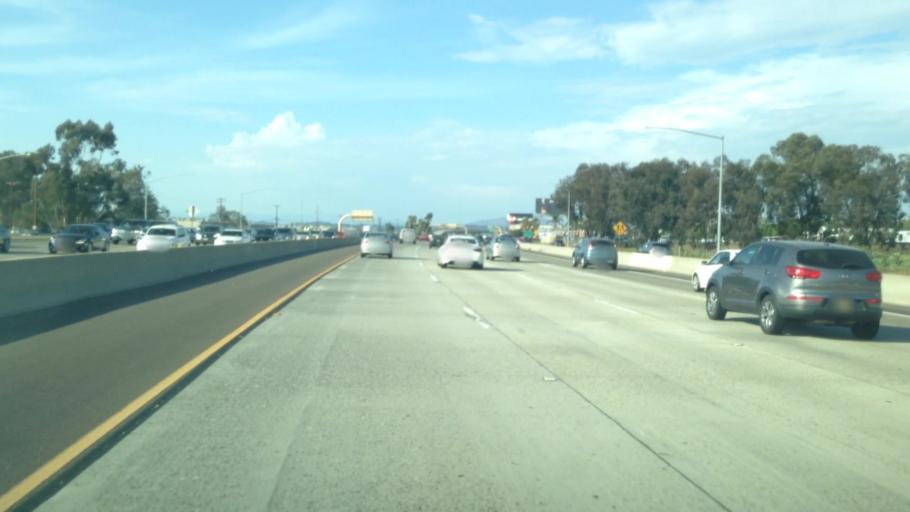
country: US
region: California
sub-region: San Diego County
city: San Diego
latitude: 32.8330
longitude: -117.1405
